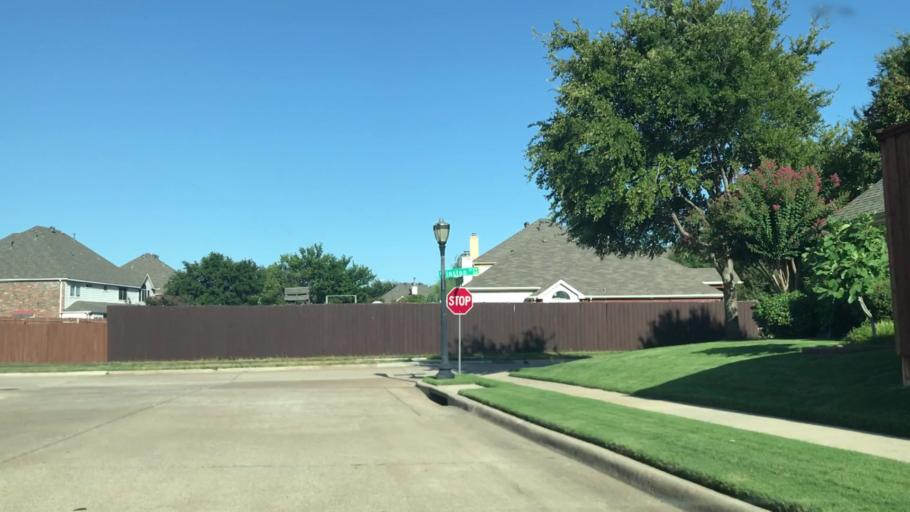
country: US
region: Texas
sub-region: Collin County
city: Frisco
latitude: 33.1342
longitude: -96.7847
